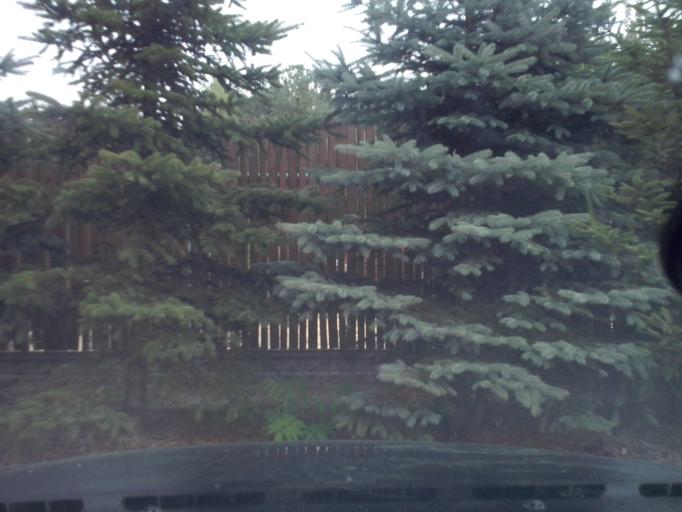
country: PL
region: Swietokrzyskie
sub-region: Powiat kielecki
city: Domaszowice
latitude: 50.8147
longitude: 20.6926
